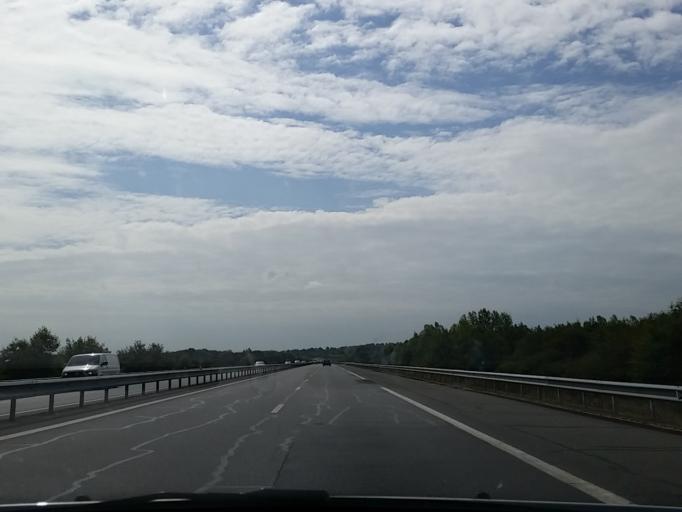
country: FR
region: Auvergne
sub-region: Departement de l'Allier
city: Vallon-en-Sully
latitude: 46.5469
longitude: 2.5518
